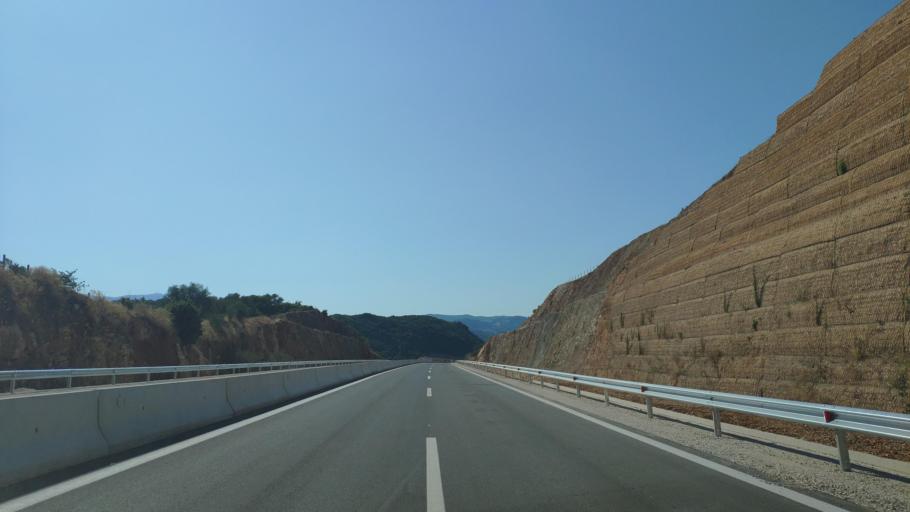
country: GR
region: West Greece
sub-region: Nomos Aitolias kai Akarnanias
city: Stanos
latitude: 38.7775
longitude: 21.1526
